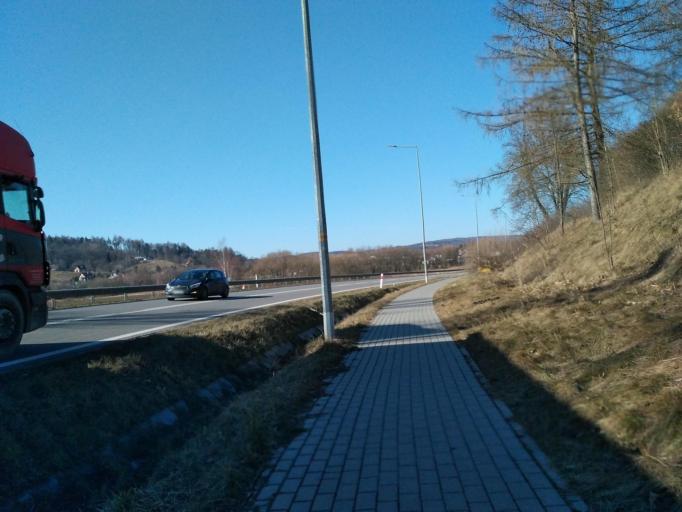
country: PL
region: Subcarpathian Voivodeship
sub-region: Powiat strzyzowski
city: Babica
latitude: 49.9357
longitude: 21.8548
